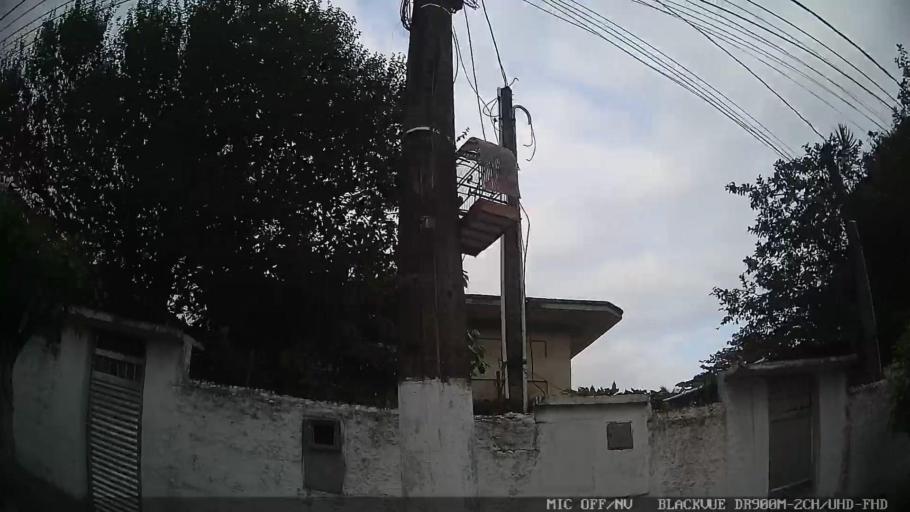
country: BR
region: Sao Paulo
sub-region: Santos
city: Santos
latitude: -23.9511
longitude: -46.2869
